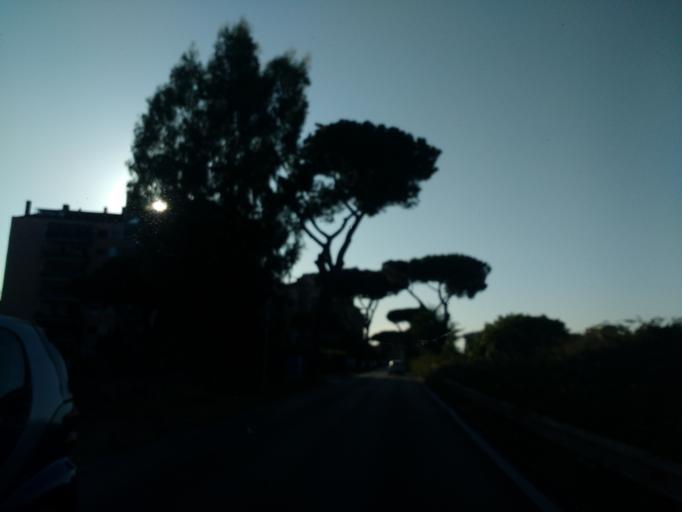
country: IT
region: Latium
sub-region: Citta metropolitana di Roma Capitale
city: Vitinia
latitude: 41.7678
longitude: 12.3783
